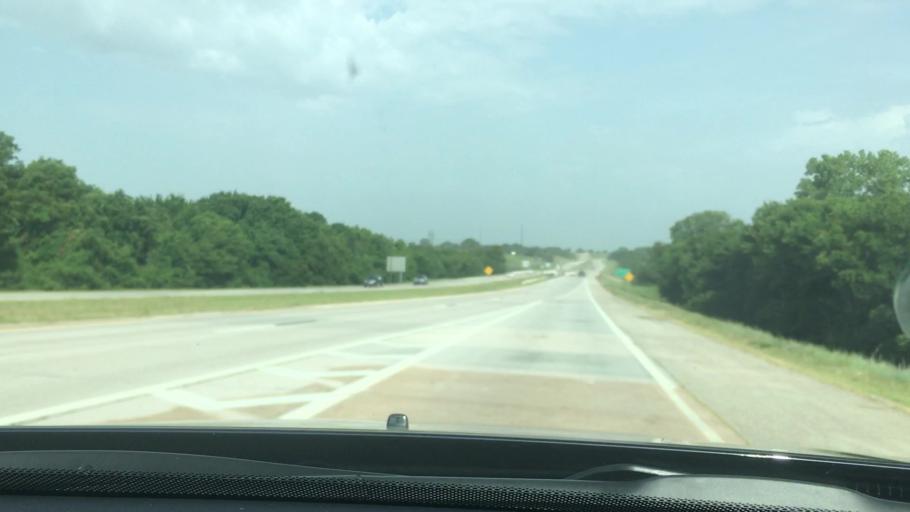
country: US
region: Oklahoma
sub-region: Pontotoc County
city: Ada
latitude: 34.7778
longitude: -96.7057
